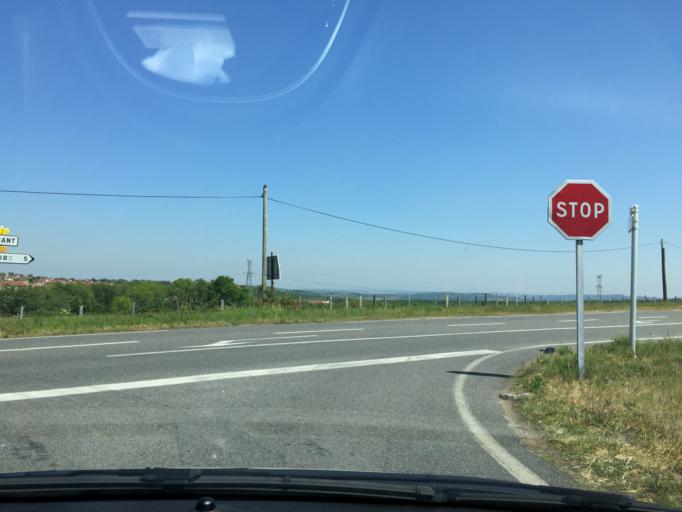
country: FR
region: Rhone-Alpes
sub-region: Departement du Rhone
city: Chassagny
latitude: 45.5935
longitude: 4.7217
